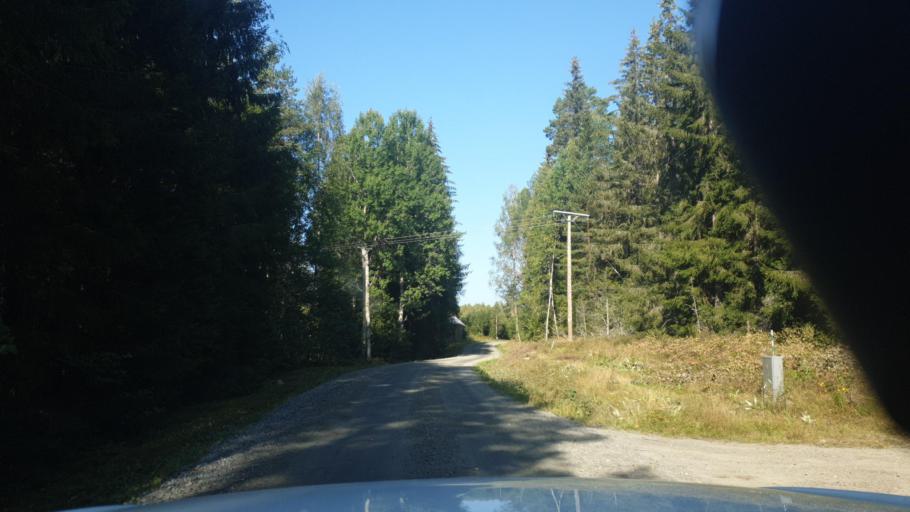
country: SE
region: Vaermland
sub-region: Sunne Kommun
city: Sunne
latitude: 59.6636
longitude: 13.0431
